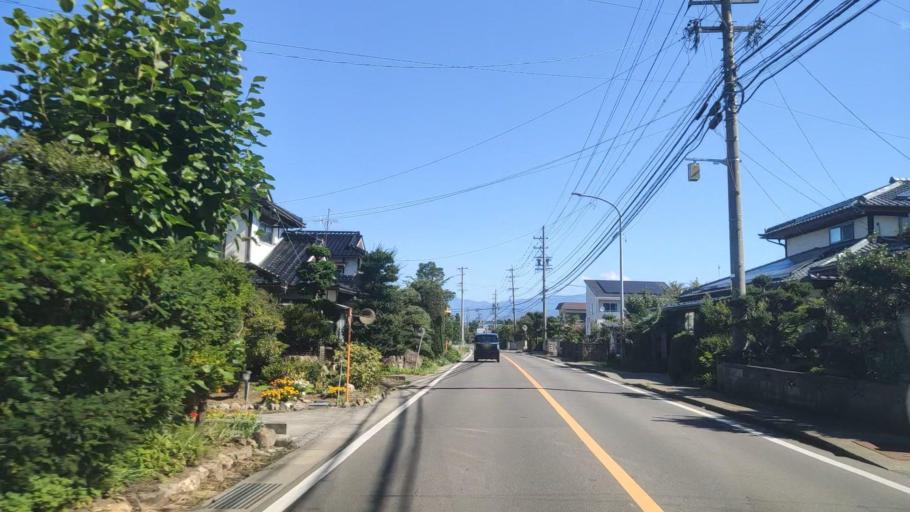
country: JP
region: Nagano
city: Shiojiri
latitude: 36.1397
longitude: 137.9396
